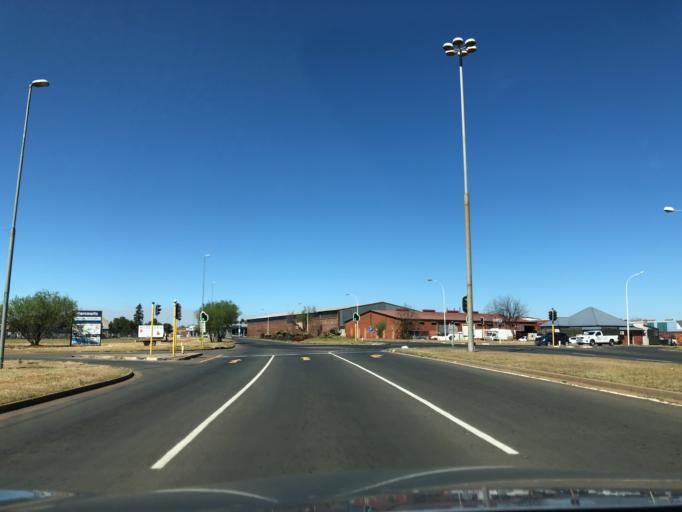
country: ZA
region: KwaZulu-Natal
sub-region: Amajuba District Municipality
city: Newcastle
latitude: -27.7504
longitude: 29.9378
